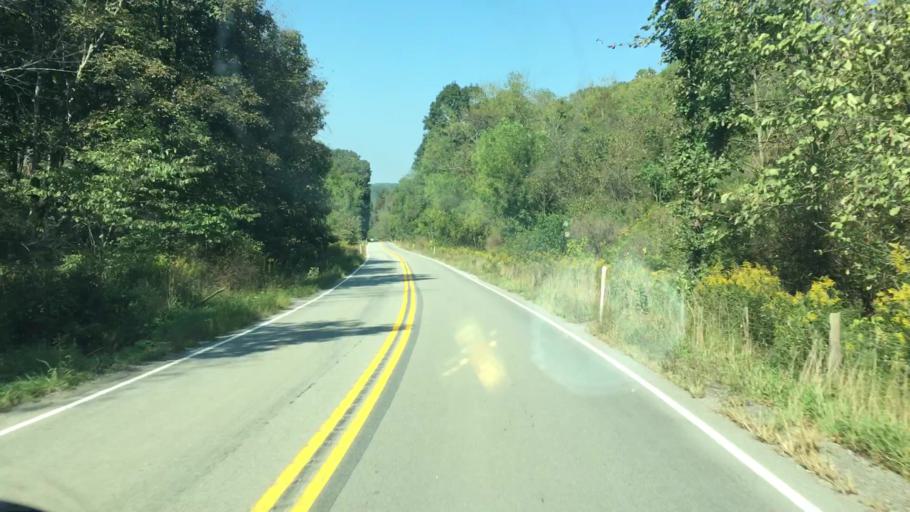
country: US
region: Pennsylvania
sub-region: Greene County
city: Waynesburg
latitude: 39.9896
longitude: -80.3473
